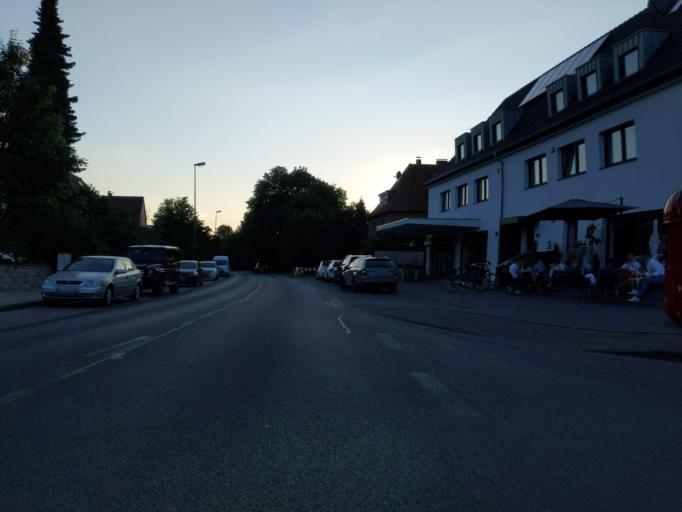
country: DE
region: North Rhine-Westphalia
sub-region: Regierungsbezirk Detmold
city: Bielefeld
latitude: 52.0228
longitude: 8.4886
